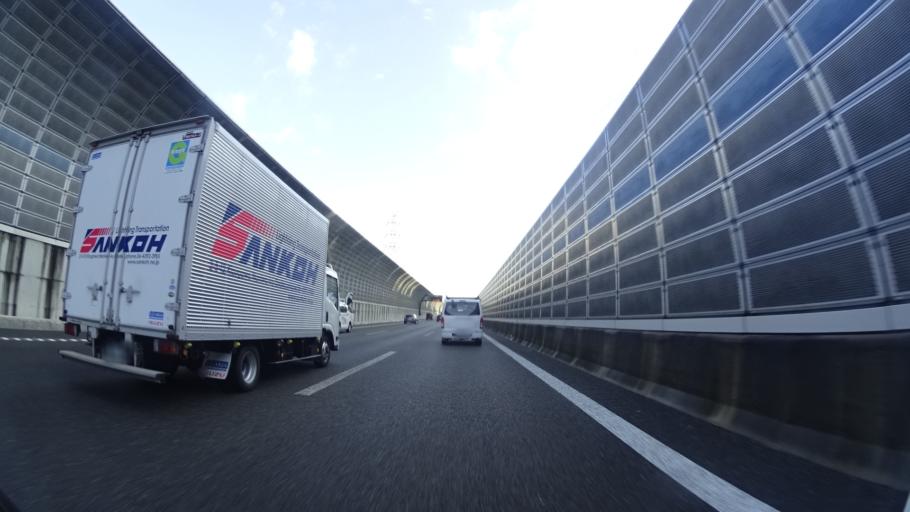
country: JP
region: Osaka
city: Hirakata
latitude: 34.8030
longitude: 135.7074
